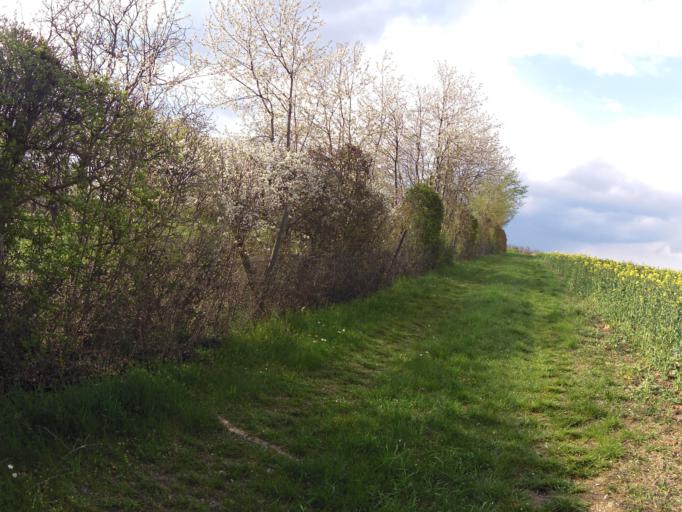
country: DE
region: Bavaria
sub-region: Regierungsbezirk Unterfranken
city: Rimpar
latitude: 49.8644
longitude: 9.9439
